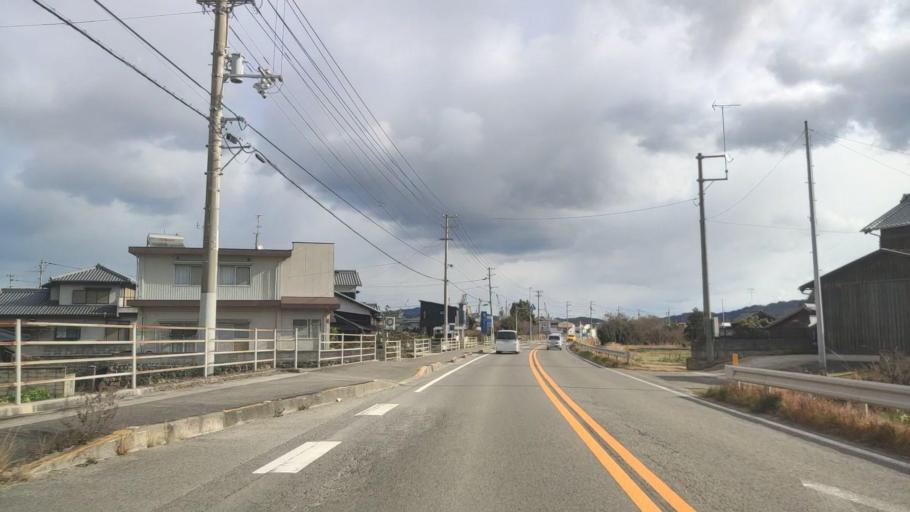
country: JP
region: Ehime
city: Hojo
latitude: 34.0642
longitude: 132.9001
